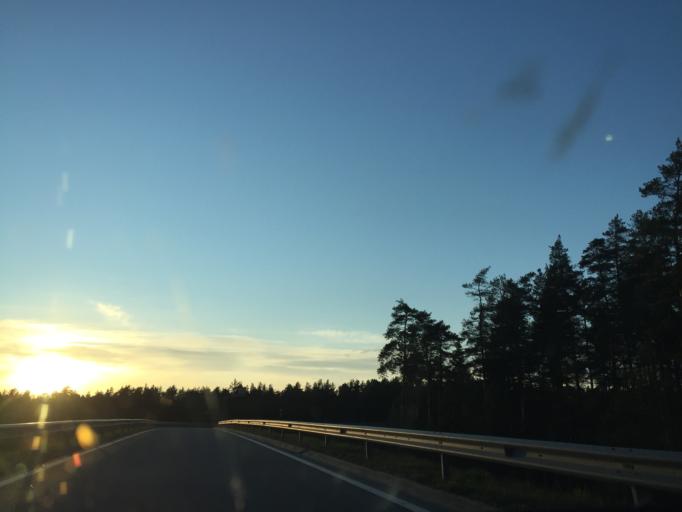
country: LV
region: Riga
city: Bergi
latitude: 57.0123
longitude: 24.3098
